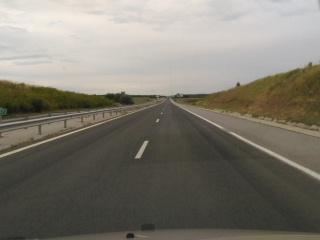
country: BG
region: Stara Zagora
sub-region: Obshtina Chirpan
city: Chirpan
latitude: 42.2630
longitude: 25.4351
